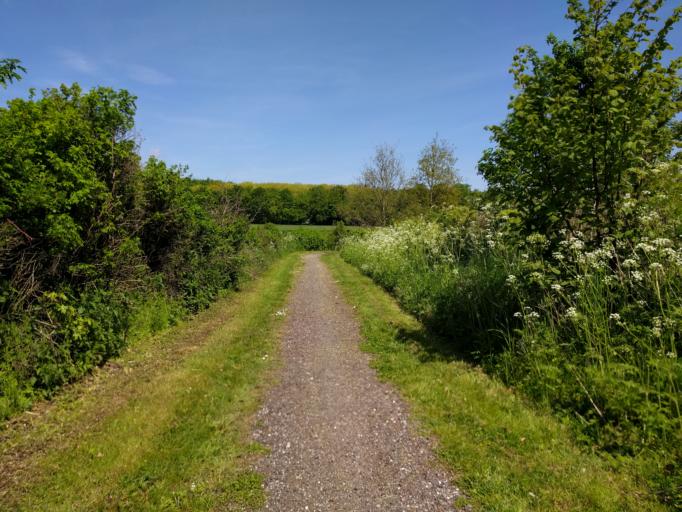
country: DK
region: Zealand
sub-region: Guldborgsund Kommune
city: Stubbekobing
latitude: 54.7581
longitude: 12.0395
